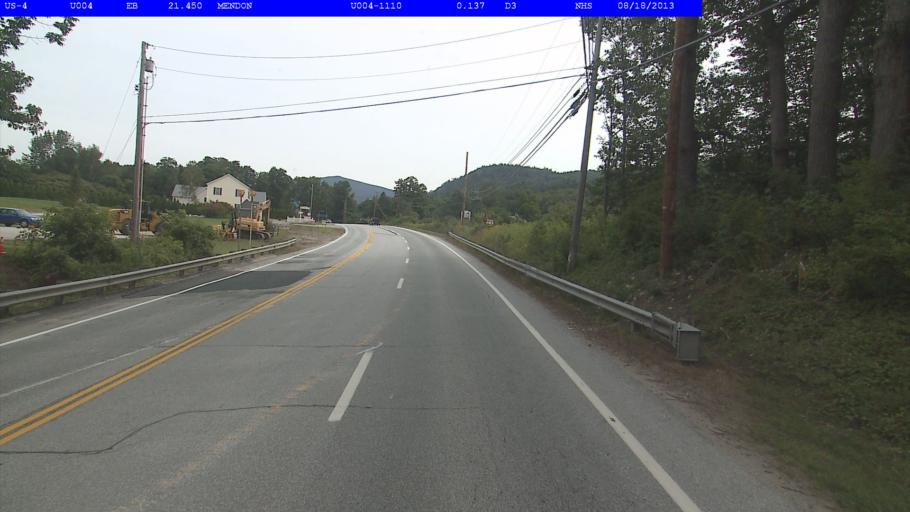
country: US
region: Vermont
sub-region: Rutland County
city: Rutland
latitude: 43.6363
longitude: -72.9354
